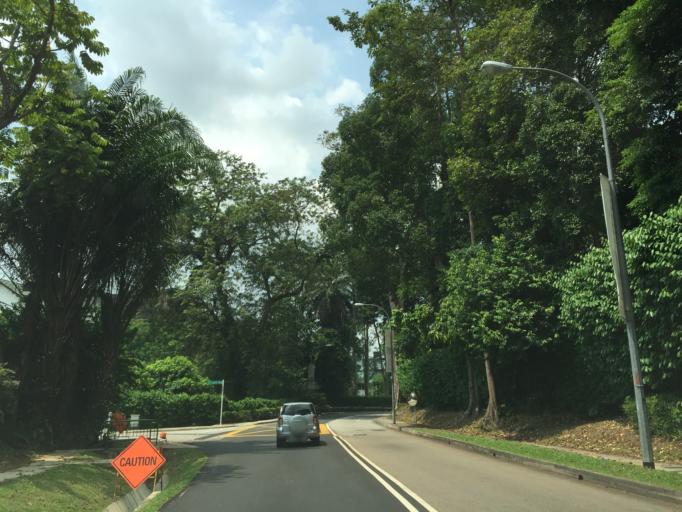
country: SG
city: Singapore
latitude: 1.3115
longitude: 103.8174
